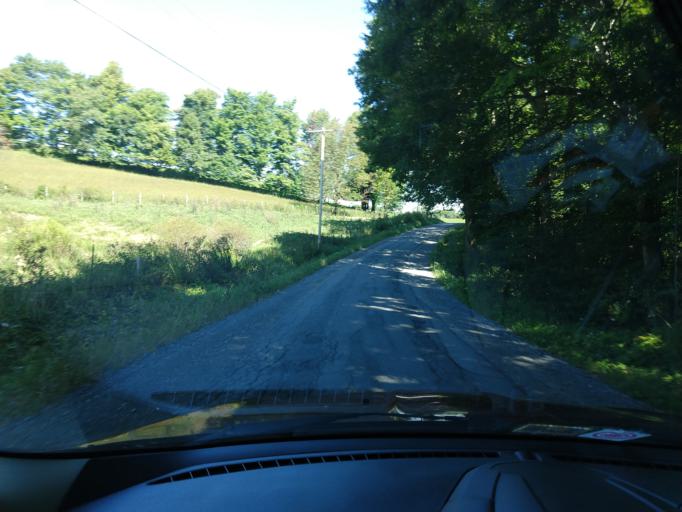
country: US
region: West Virginia
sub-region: Nicholas County
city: Craigsville
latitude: 38.2413
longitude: -80.7087
